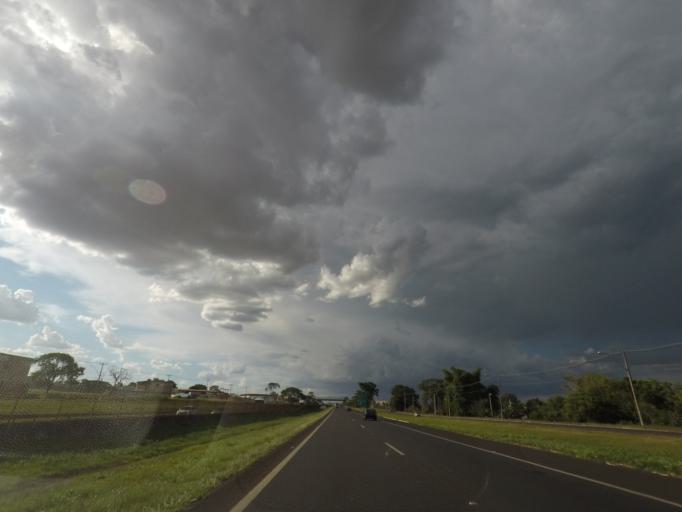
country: BR
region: Sao Paulo
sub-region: Ribeirao Preto
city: Ribeirao Preto
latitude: -21.1315
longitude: -47.7667
